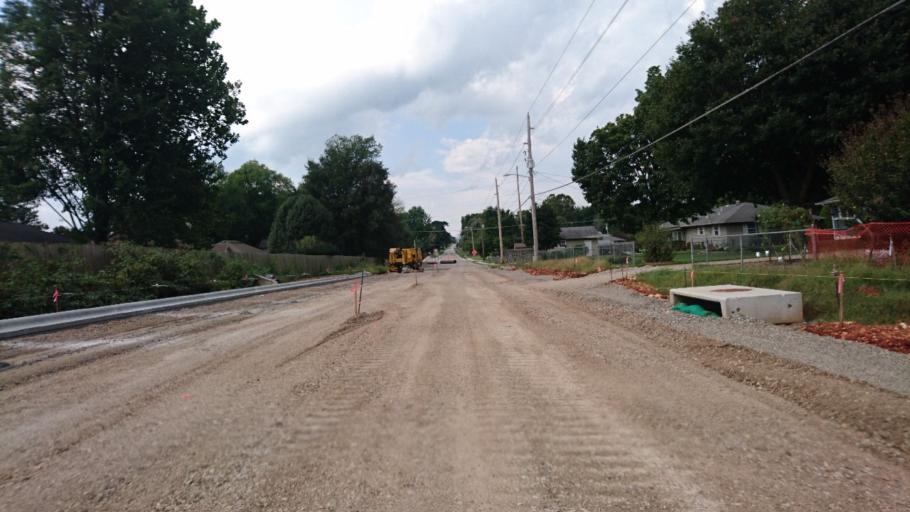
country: US
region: Missouri
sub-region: Greene County
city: Springfield
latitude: 37.2050
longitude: -93.3609
